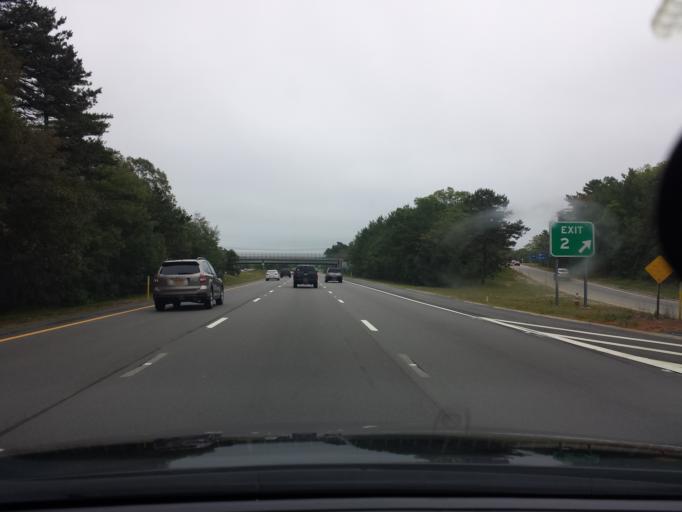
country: US
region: Massachusetts
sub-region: Plymouth County
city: Onset
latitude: 41.7686
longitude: -70.6838
